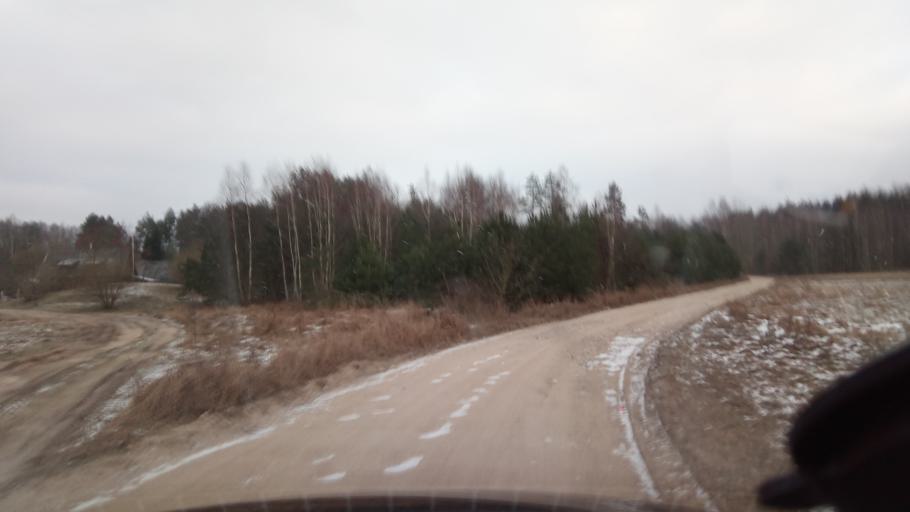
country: LT
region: Alytaus apskritis
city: Varena
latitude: 54.1214
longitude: 24.7042
